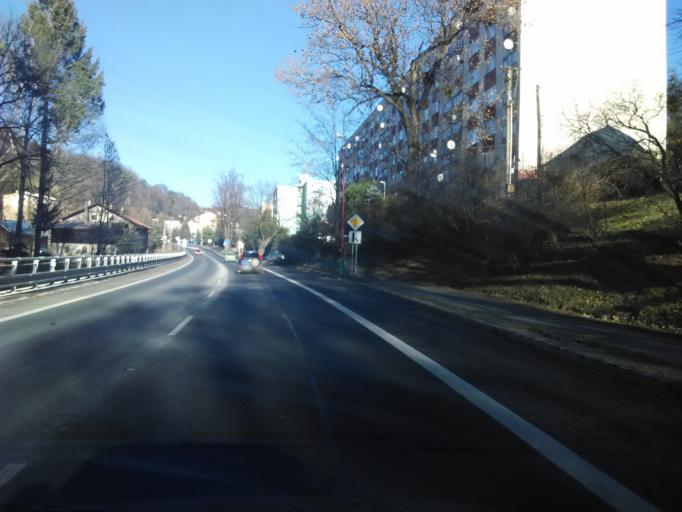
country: SK
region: Banskobystricky
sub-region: Okres Ziar nad Hronom
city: Kremnica
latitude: 48.6966
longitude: 18.9153
